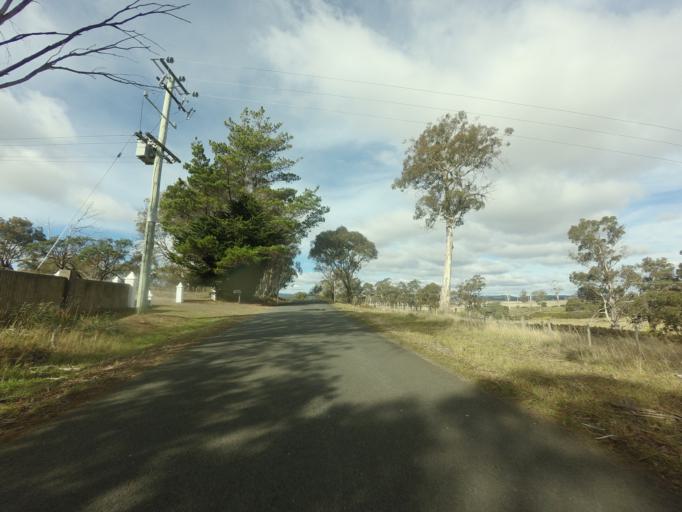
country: AU
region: Tasmania
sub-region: Brighton
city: Bridgewater
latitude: -42.3982
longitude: 147.3790
